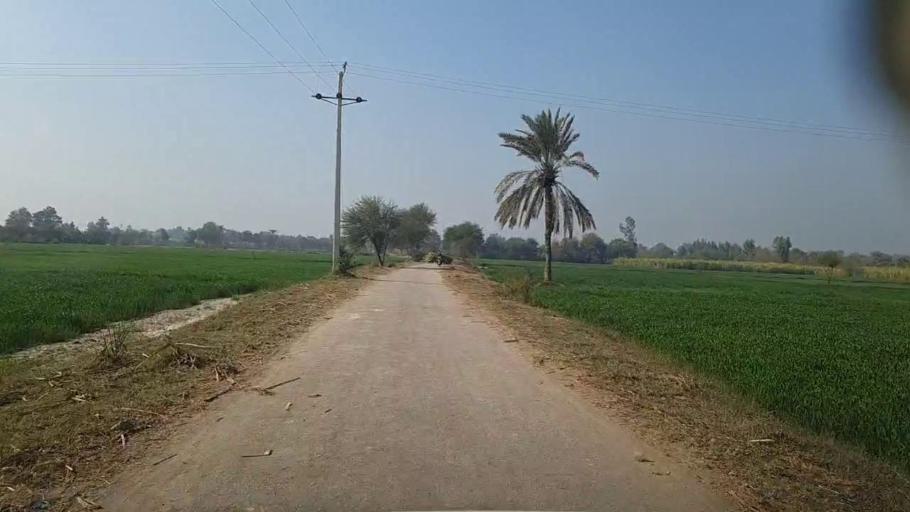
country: PK
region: Sindh
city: Mirpur Mathelo
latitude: 27.9239
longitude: 69.6579
